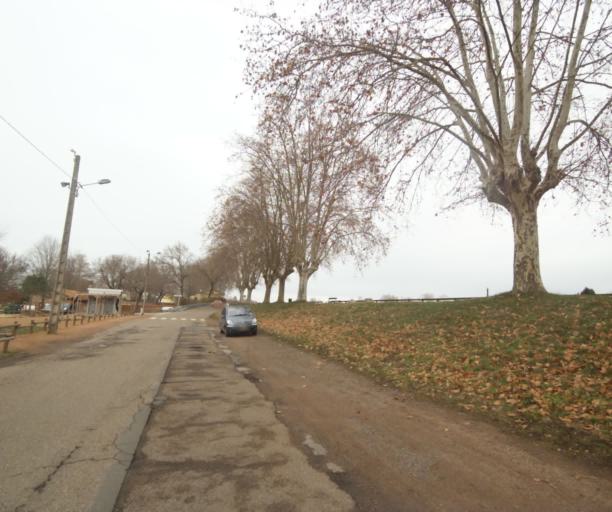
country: FR
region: Rhone-Alpes
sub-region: Departement de la Loire
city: Le Coteau
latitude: 46.0388
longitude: 4.0843
